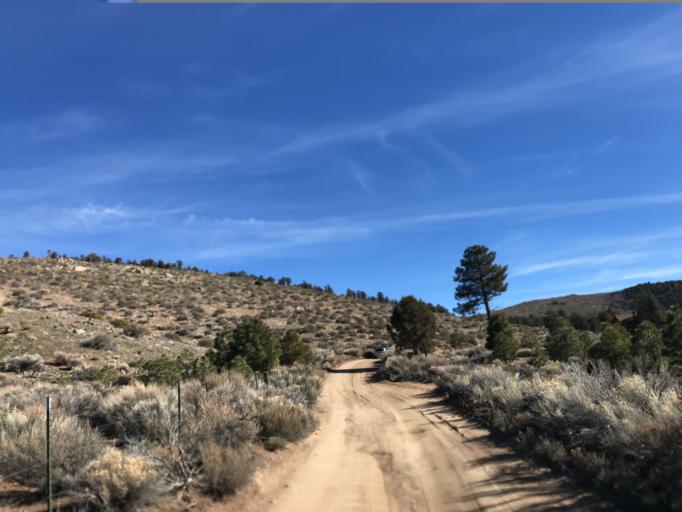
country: US
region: California
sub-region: San Bernardino County
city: Big Bear City
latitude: 34.2801
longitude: -116.7955
